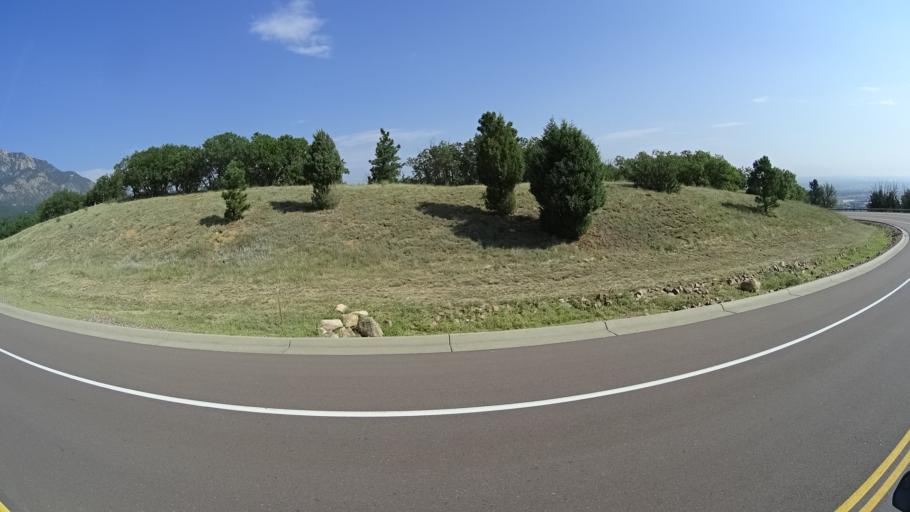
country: US
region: Colorado
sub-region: El Paso County
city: Fort Carson
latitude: 38.7478
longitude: -104.8202
